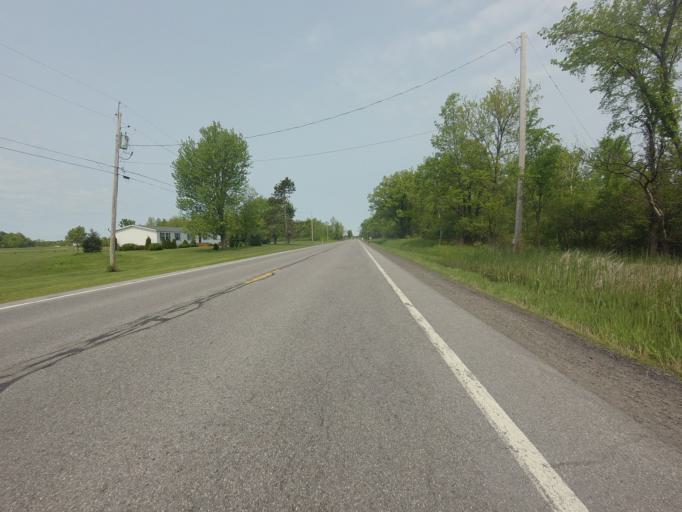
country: US
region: New York
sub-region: Jefferson County
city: Dexter
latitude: 44.0204
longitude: -76.0318
